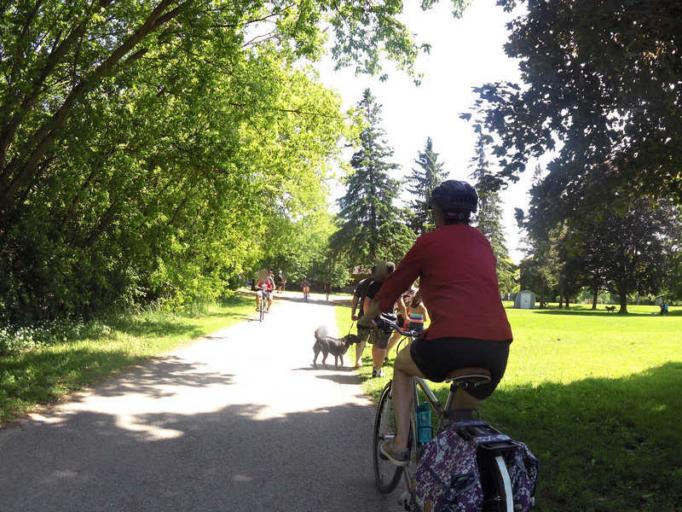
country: CA
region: Ontario
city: Peterborough
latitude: 44.2960
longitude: -78.3023
